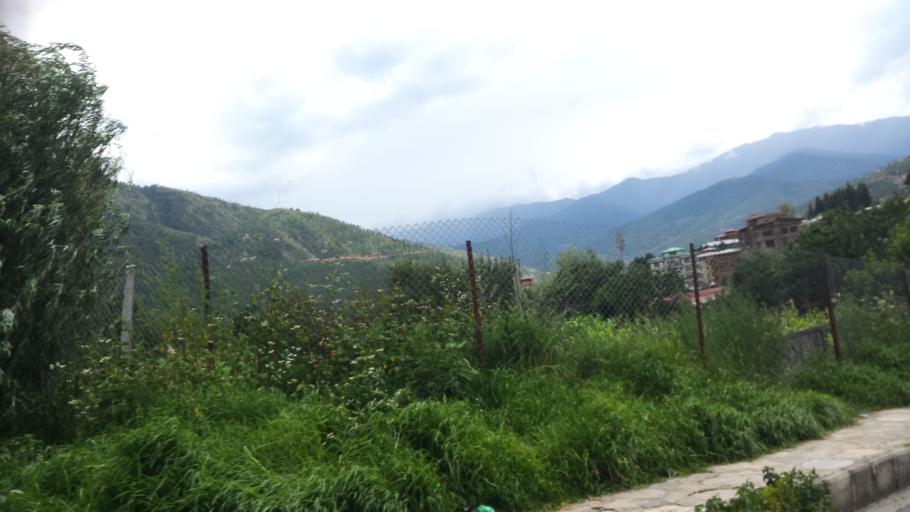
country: BT
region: Thimphu
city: Thimphu
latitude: 27.4726
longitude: 89.6317
